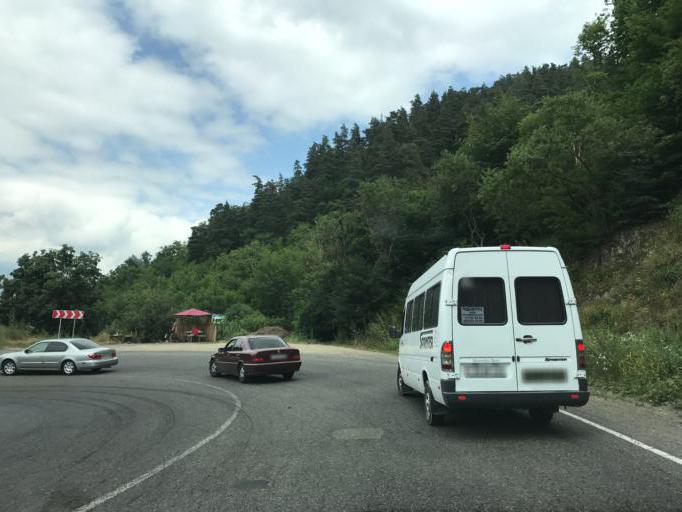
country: AM
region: Tavush
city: Dilijan
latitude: 40.7013
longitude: 44.8544
